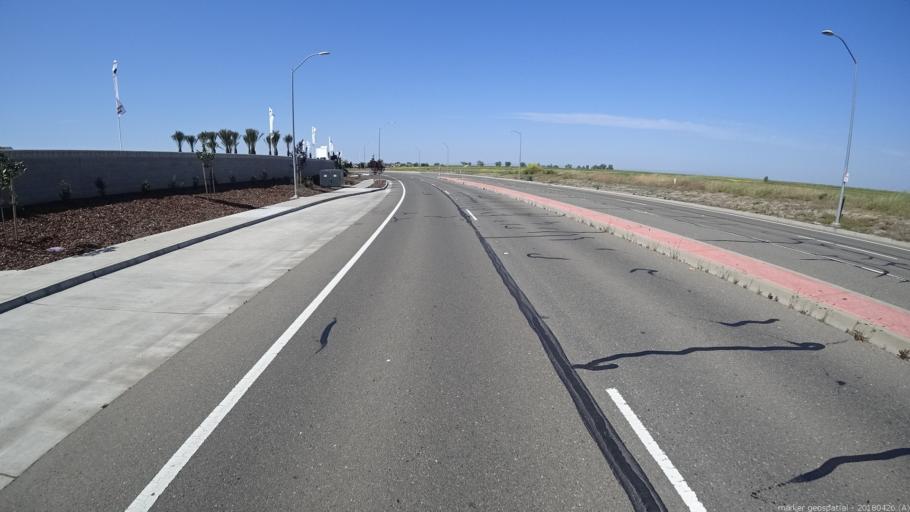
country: US
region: California
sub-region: Yolo County
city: West Sacramento
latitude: 38.5443
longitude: -121.5741
